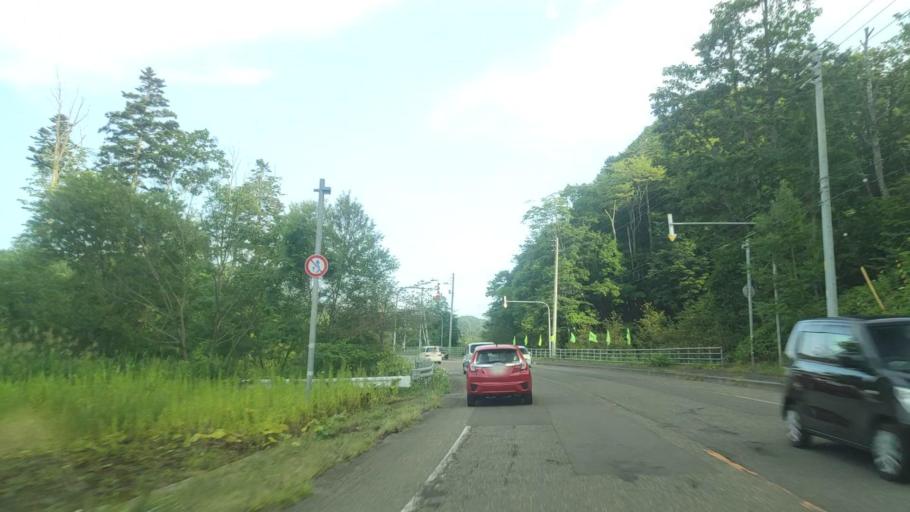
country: JP
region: Hokkaido
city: Iwamizawa
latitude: 43.0223
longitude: 141.9454
